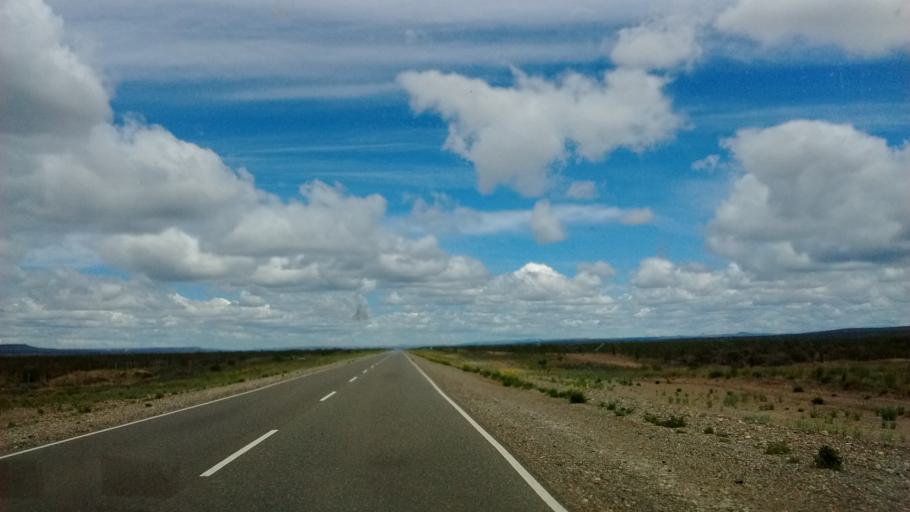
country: AR
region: Neuquen
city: Piedra del Aguila
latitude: -39.8038
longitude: -69.7008
